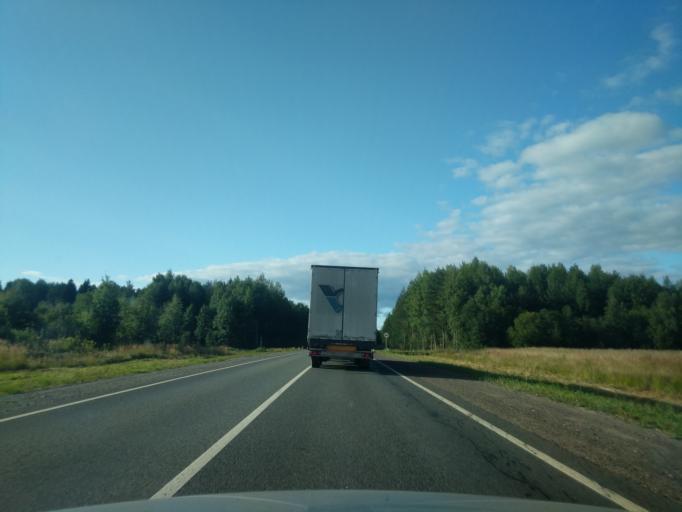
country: RU
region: Kostroma
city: Manturovo
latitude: 58.3124
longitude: 44.7210
